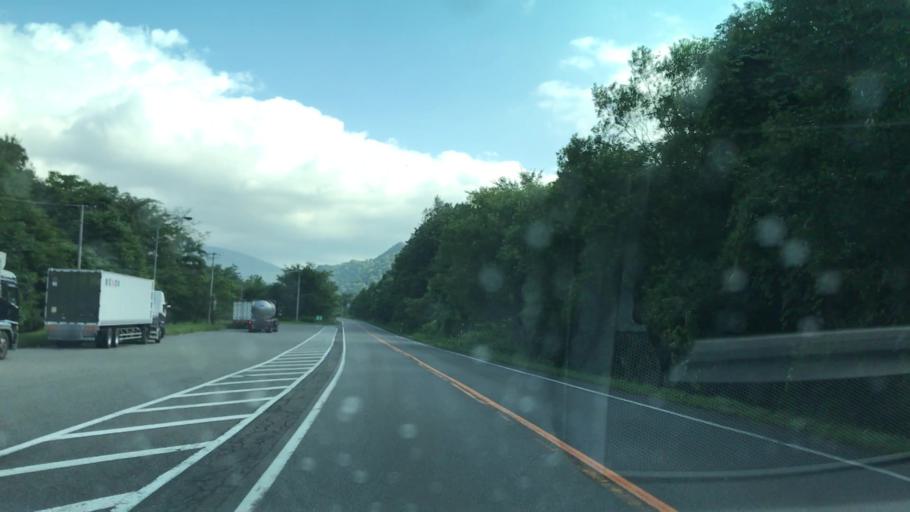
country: JP
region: Hokkaido
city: Shizunai-furukawacho
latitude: 42.8384
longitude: 142.4157
